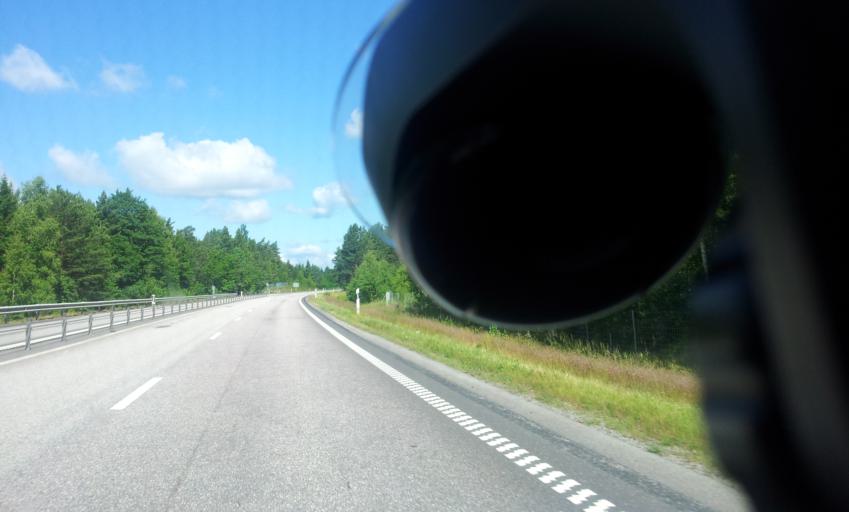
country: SE
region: Kalmar
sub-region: Oskarshamns Kommun
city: Paskallavik
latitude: 57.1291
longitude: 16.4785
